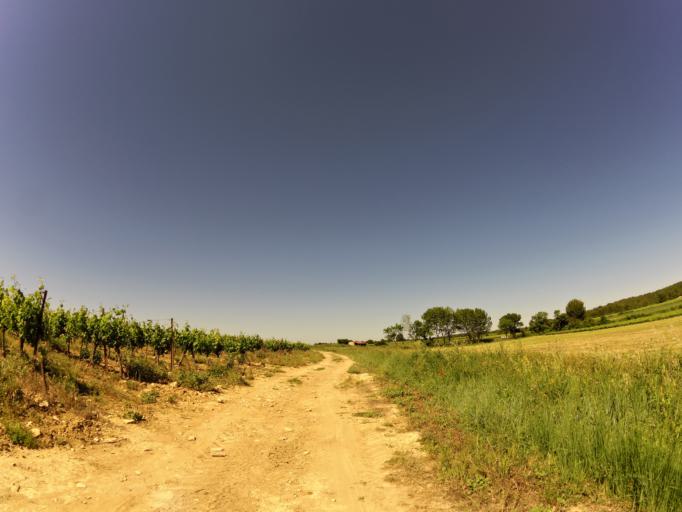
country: FR
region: Languedoc-Roussillon
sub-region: Departement du Gard
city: Mus
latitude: 43.7513
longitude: 4.1977
